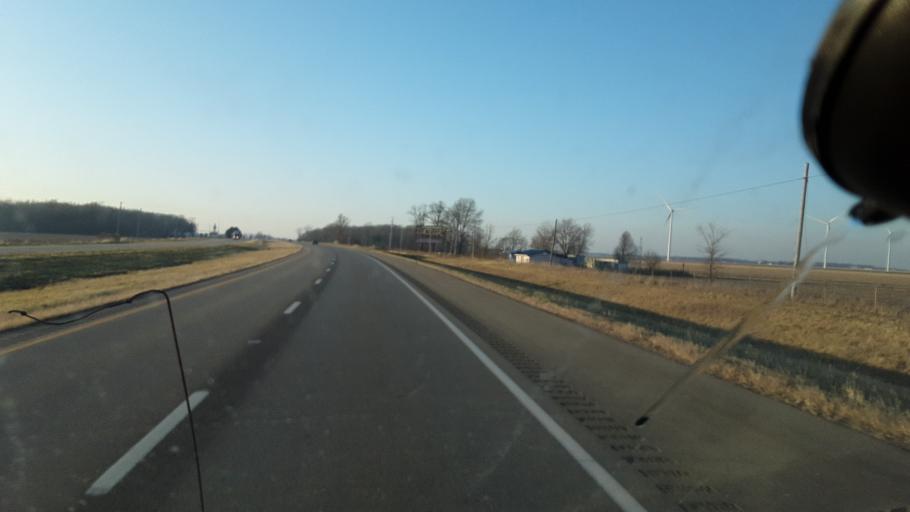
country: US
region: Indiana
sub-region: Allen County
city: Monroeville
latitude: 40.9914
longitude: -84.7864
